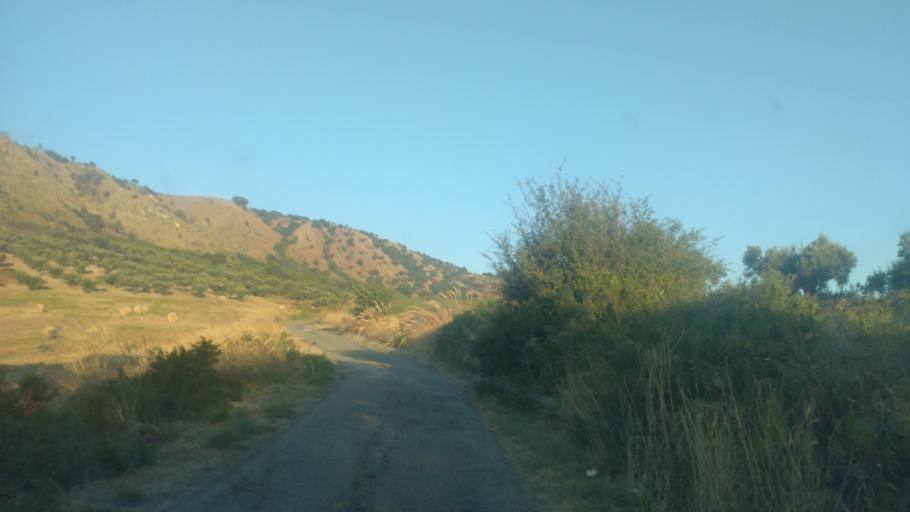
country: IT
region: Calabria
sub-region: Provincia di Catanzaro
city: Staletti
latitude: 38.7724
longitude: 16.5538
